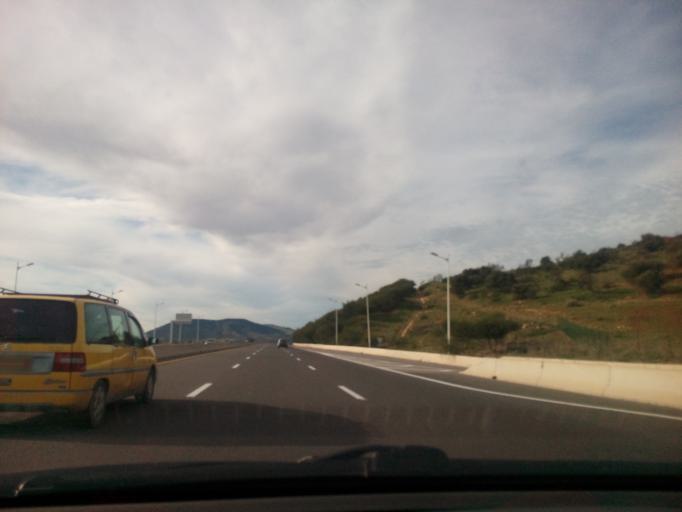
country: DZ
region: Sidi Bel Abbes
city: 'Ain el Berd
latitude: 35.4307
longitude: -0.4591
